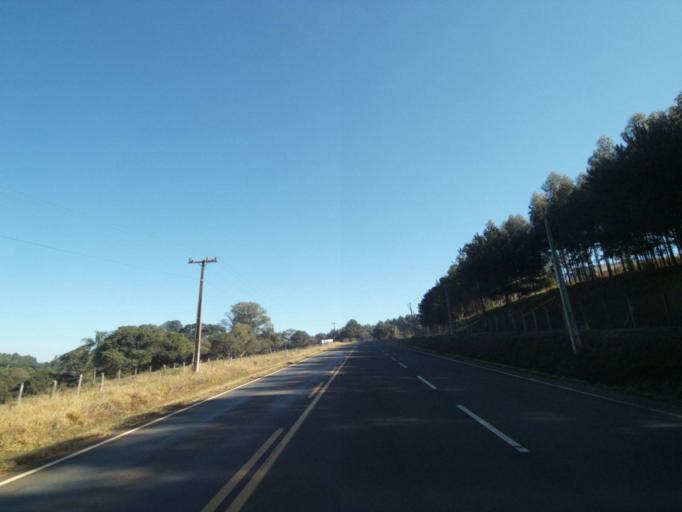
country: BR
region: Parana
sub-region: Tibagi
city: Tibagi
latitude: -24.5139
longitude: -50.4295
